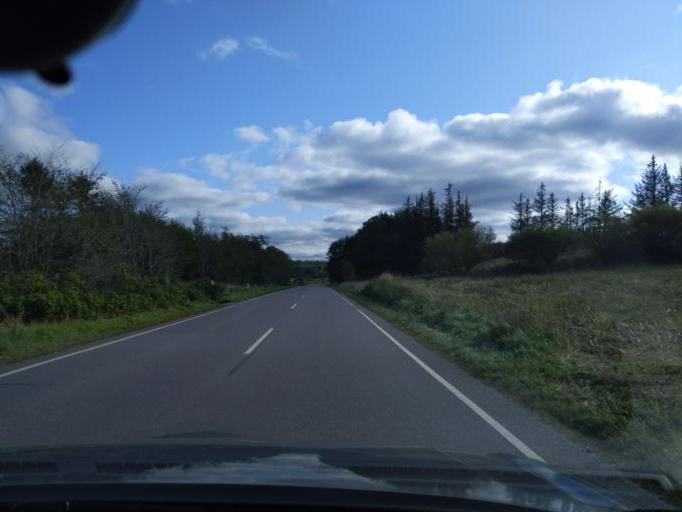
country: DK
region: North Denmark
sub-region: Mariagerfjord Kommune
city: Hobro
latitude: 56.5573
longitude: 9.7255
